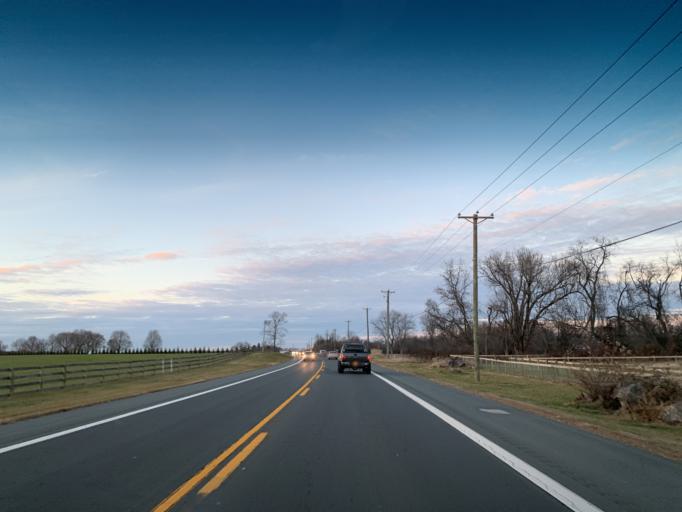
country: US
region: Maryland
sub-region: Cecil County
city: Elkton
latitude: 39.4782
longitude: -75.8481
